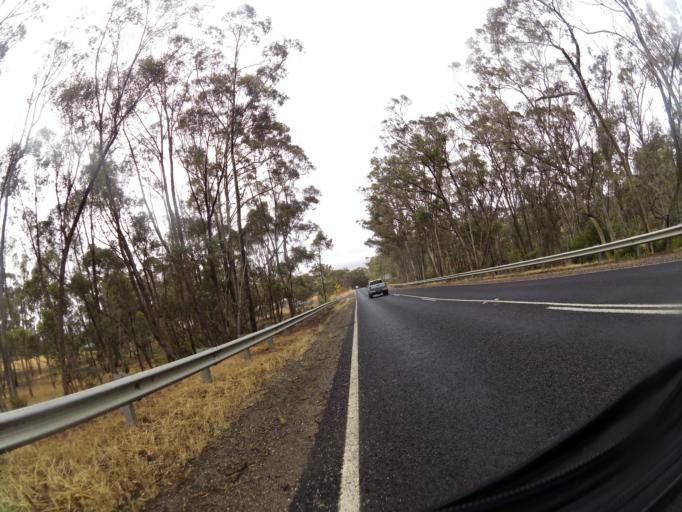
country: AU
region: Victoria
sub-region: Mount Alexander
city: Castlemaine
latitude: -37.0719
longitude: 144.1709
